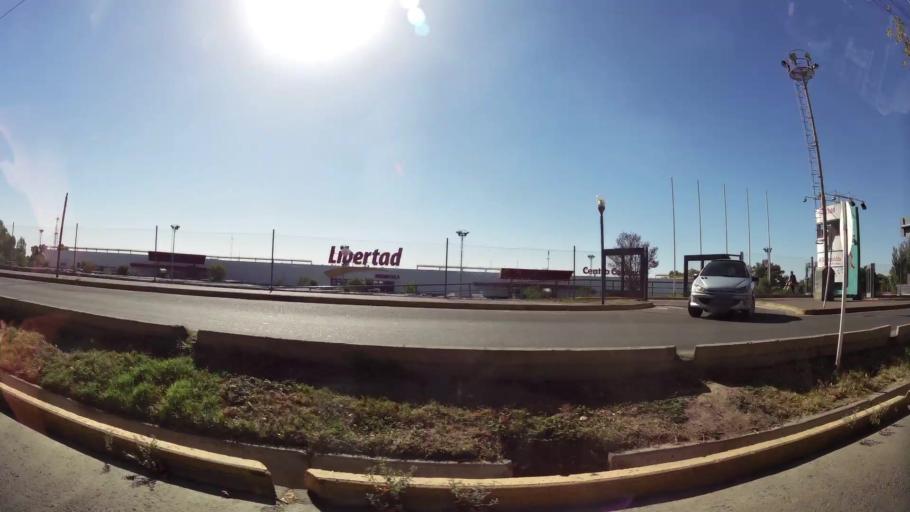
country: AR
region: Mendoza
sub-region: Departamento de Godoy Cruz
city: Godoy Cruz
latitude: -32.9295
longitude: -68.8584
